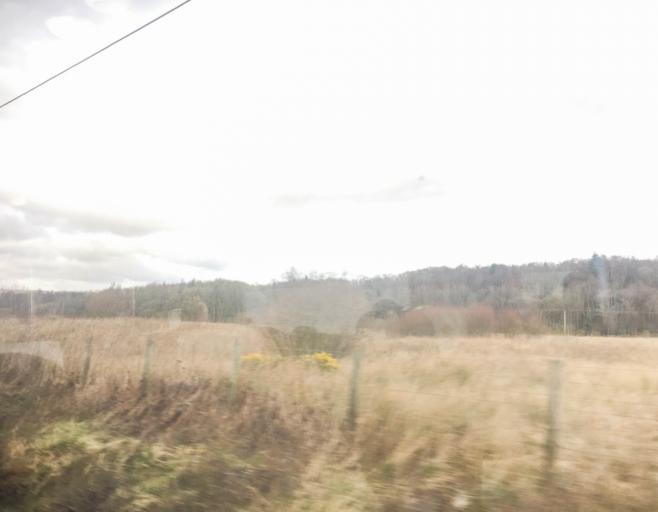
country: GB
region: Scotland
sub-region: Argyll and Bute
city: Helensburgh
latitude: 55.9888
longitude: -4.6966
